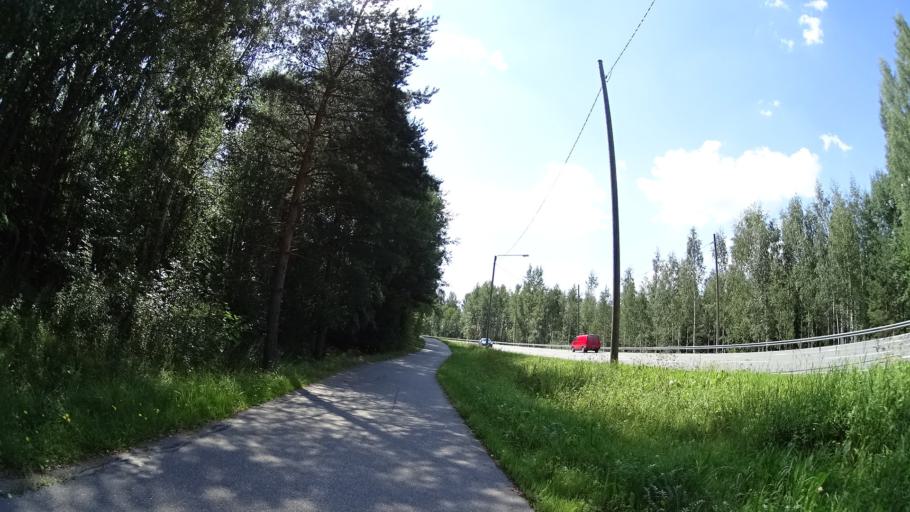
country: FI
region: Uusimaa
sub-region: Helsinki
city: Tuusula
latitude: 60.3467
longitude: 25.0035
